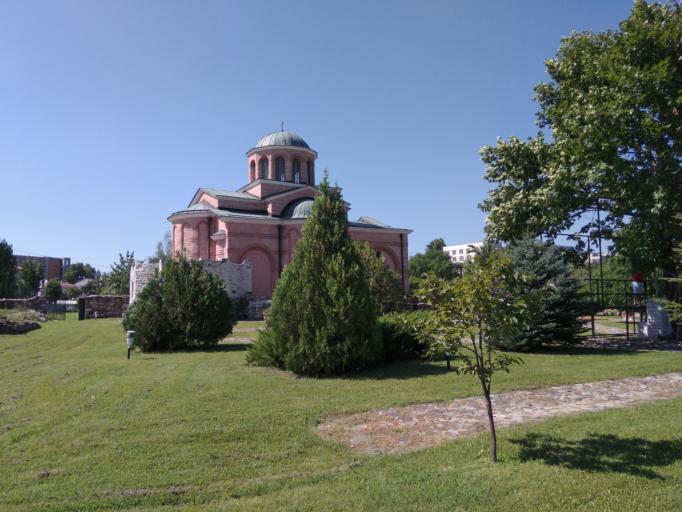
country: BG
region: Kurdzhali
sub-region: Obshtina Kurdzhali
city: Kurdzhali
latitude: 41.6268
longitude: 25.3704
